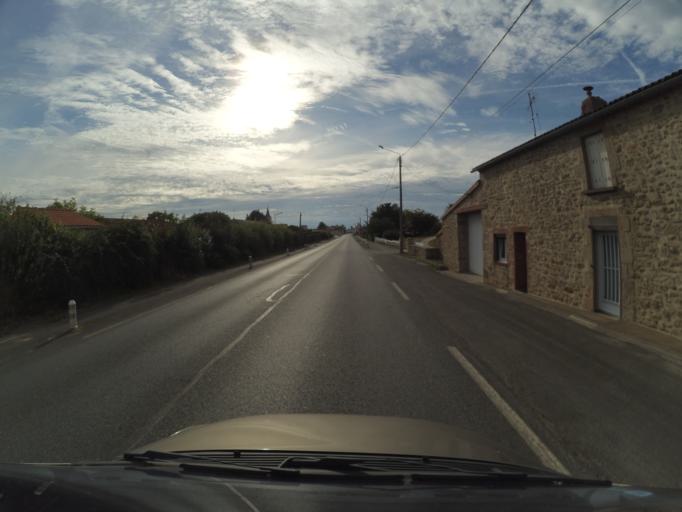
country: FR
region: Poitou-Charentes
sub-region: Departement des Deux-Sevres
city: Saint-Amand-sur-Sevre
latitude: 46.9286
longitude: -0.8126
